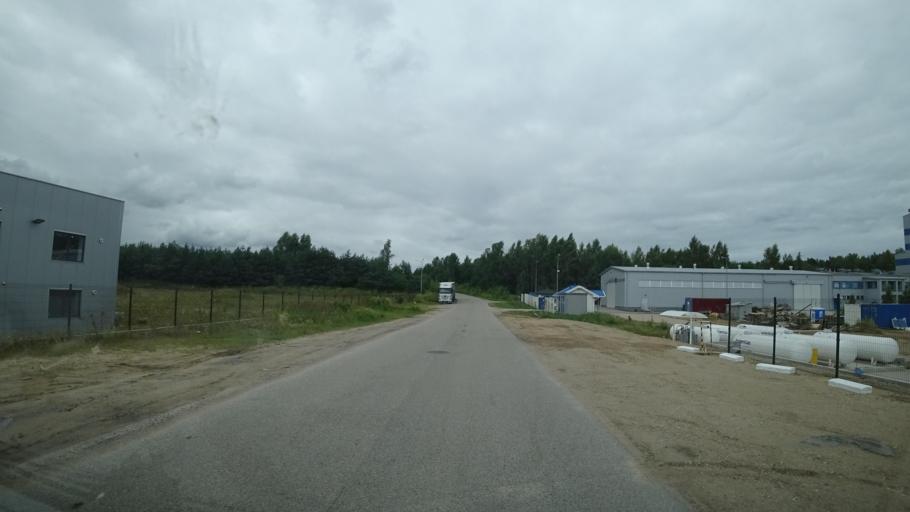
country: PL
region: Warmian-Masurian Voivodeship
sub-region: Powiat goldapski
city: Goldap
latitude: 54.3347
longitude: 22.2924
